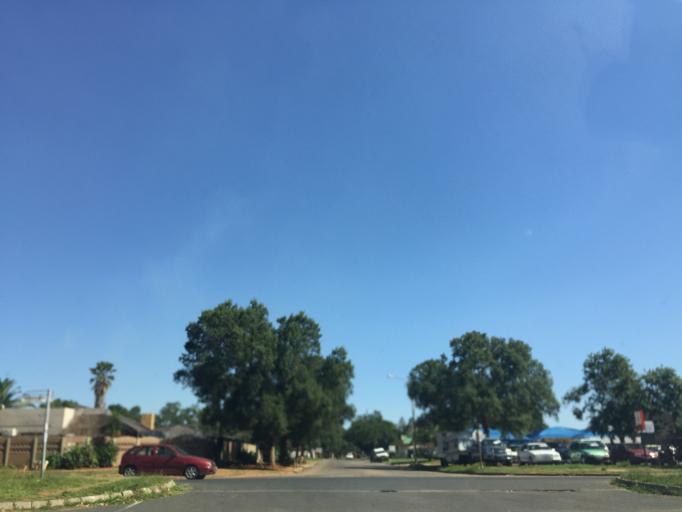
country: ZA
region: Gauteng
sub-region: Sedibeng District Municipality
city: Vanderbijlpark
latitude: -26.6973
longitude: 27.8434
